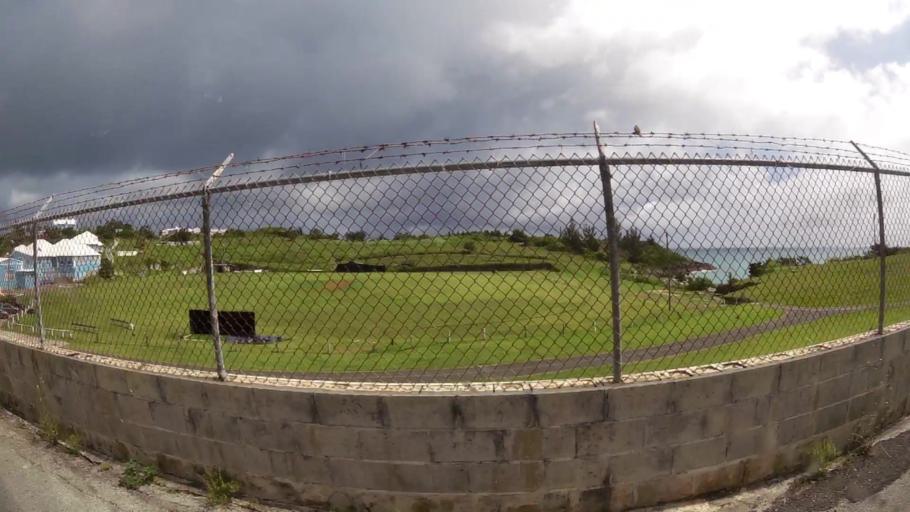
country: BM
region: Saint George
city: Saint George
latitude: 32.3691
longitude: -64.6511
